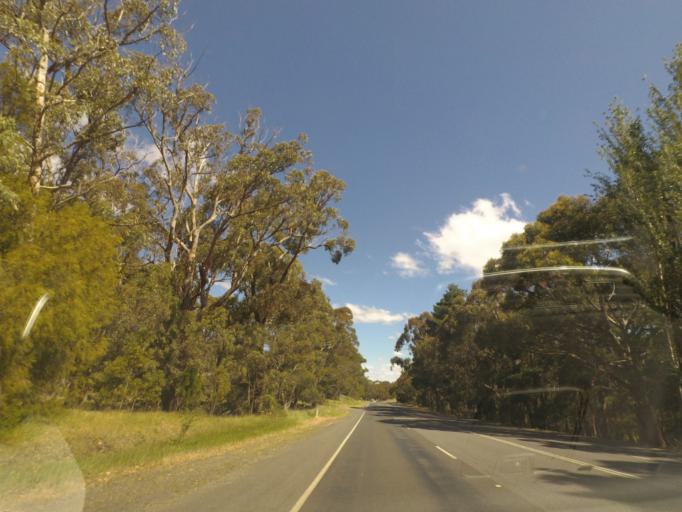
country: AU
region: Victoria
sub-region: Hume
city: Sunbury
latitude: -37.4216
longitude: 144.5533
